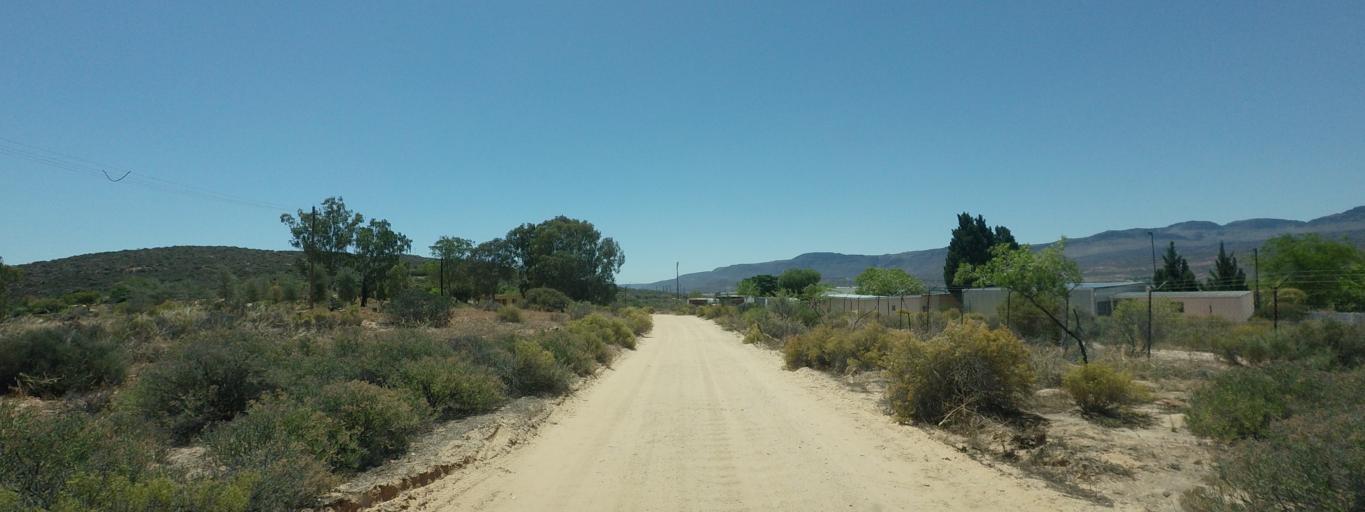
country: ZA
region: Western Cape
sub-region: West Coast District Municipality
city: Clanwilliam
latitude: -32.1875
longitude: 18.8847
